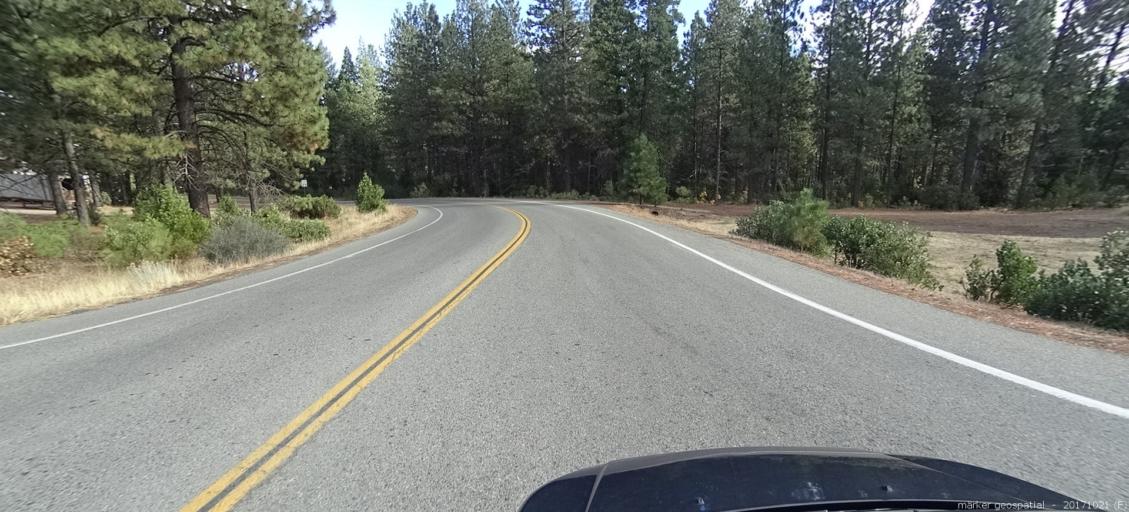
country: US
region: California
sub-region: Shasta County
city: Burney
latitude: 40.8758
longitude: -121.6790
